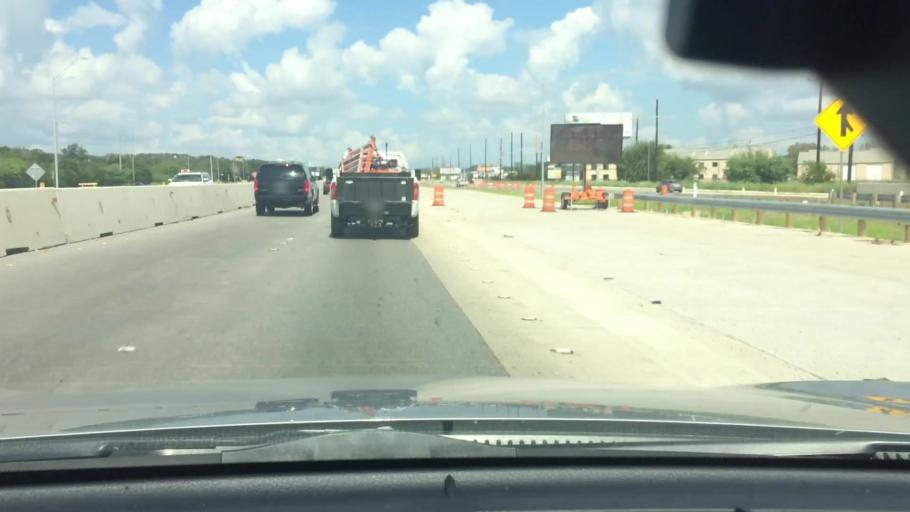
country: US
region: Texas
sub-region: Bexar County
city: Scenic Oaks
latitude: 29.6892
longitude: -98.6449
